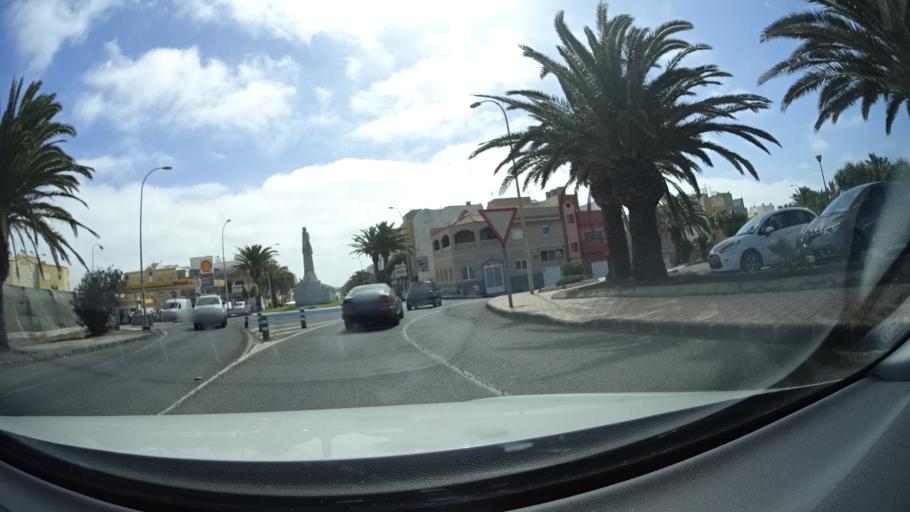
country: ES
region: Canary Islands
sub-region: Provincia de Las Palmas
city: Cruce de Arinaga
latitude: 27.8598
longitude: -15.4000
